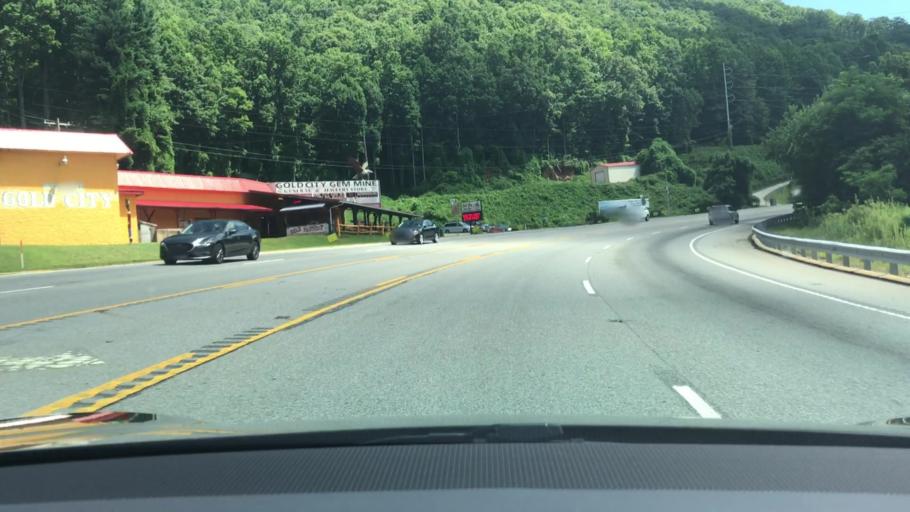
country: US
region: North Carolina
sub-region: Macon County
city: Franklin
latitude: 35.2592
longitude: -83.3161
